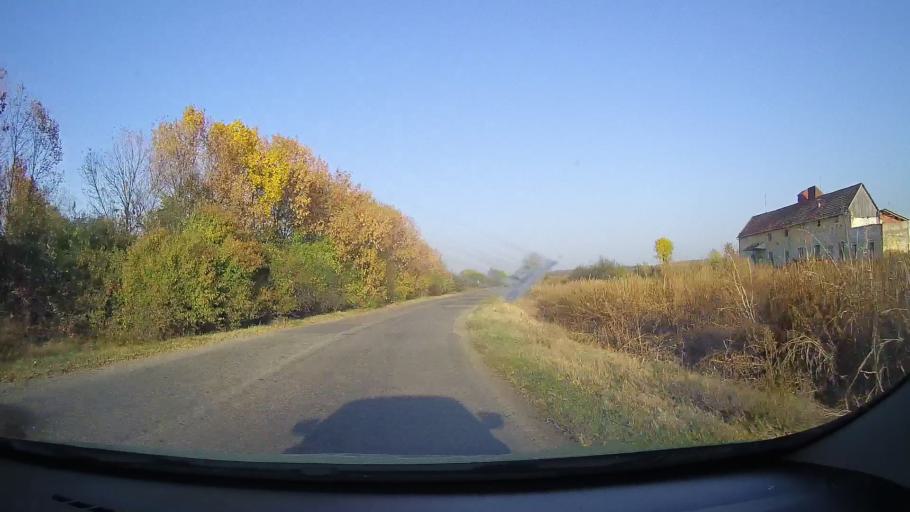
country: RO
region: Arad
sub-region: Comuna Tarnova
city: Tarnova
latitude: 46.3191
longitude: 21.8061
